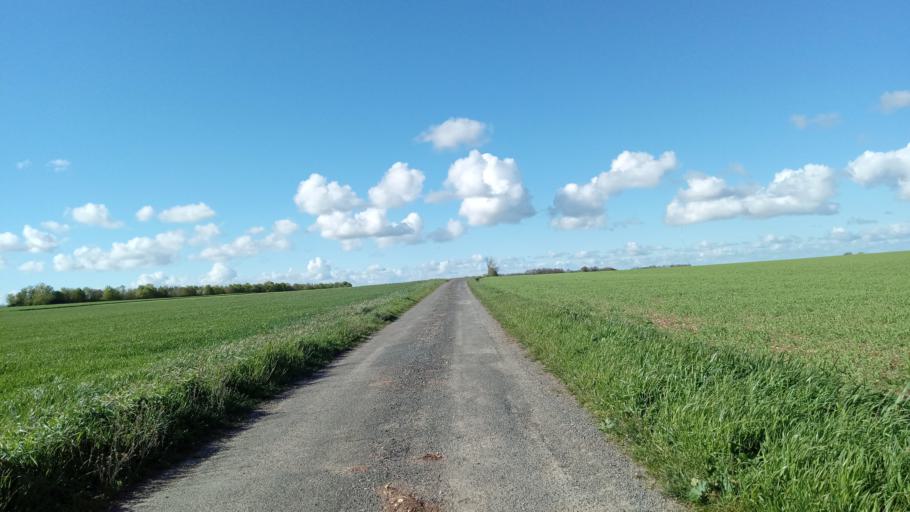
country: FR
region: Poitou-Charentes
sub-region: Departement de la Charente-Maritime
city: Verines
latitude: 46.1553
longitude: -0.9337
